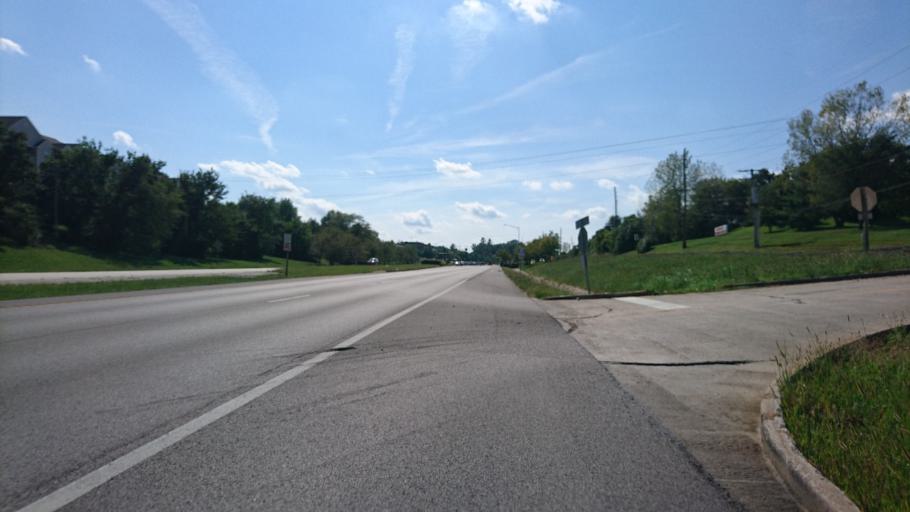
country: US
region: Missouri
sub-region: Saint Louis County
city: Ellisville
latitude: 38.5854
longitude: -90.6124
